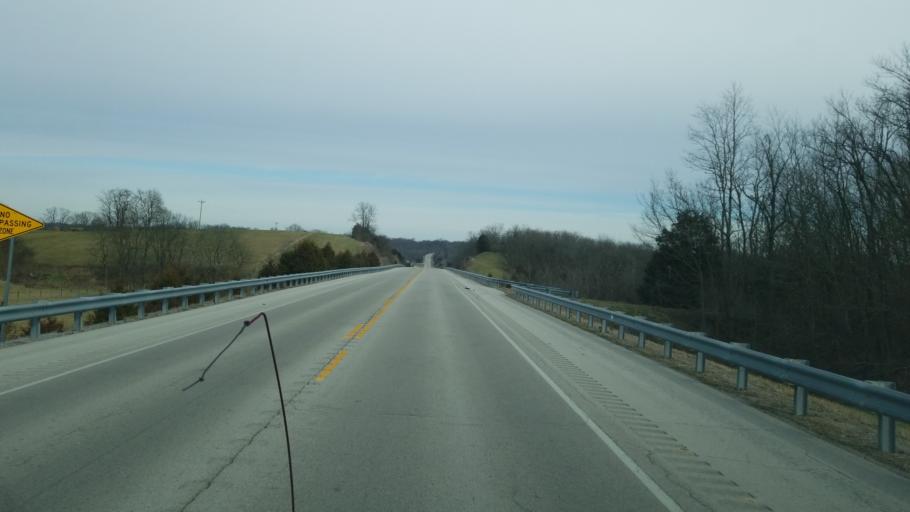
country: US
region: Kentucky
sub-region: Robertson County
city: Mount Olivet
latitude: 38.4661
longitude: -83.9141
